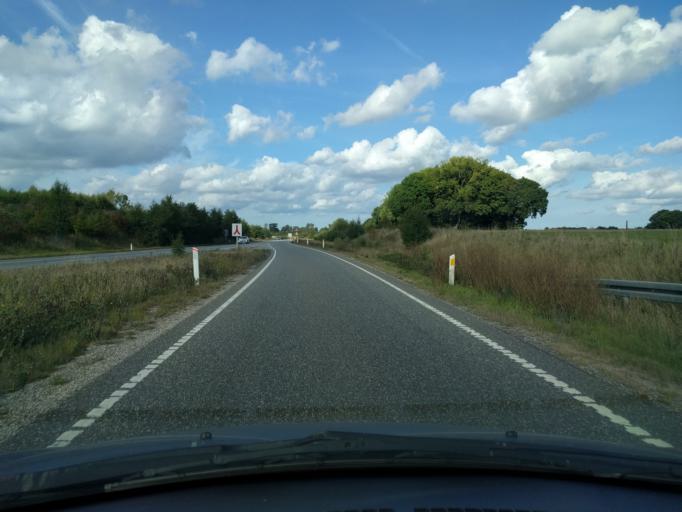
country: DK
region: South Denmark
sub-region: Odense Kommune
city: Neder Holluf
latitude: 55.3779
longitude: 10.4796
